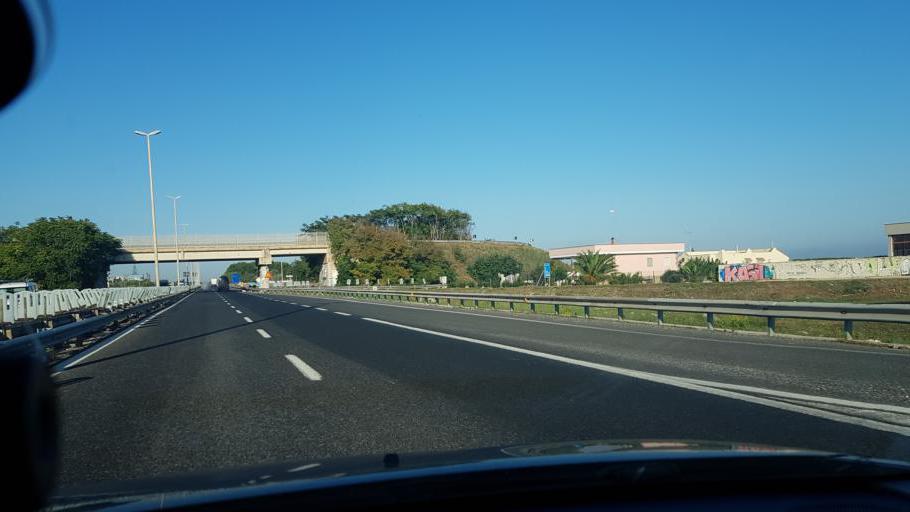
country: IT
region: Apulia
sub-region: Provincia di Bari
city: Parco Scizzo-Parchitello
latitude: 41.0805
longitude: 17.0298
